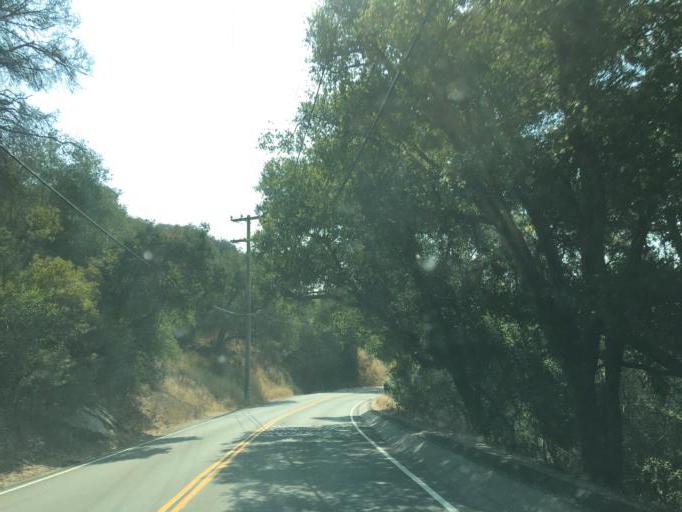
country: US
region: California
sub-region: Los Angeles County
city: Topanga
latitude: 34.0939
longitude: -118.6108
